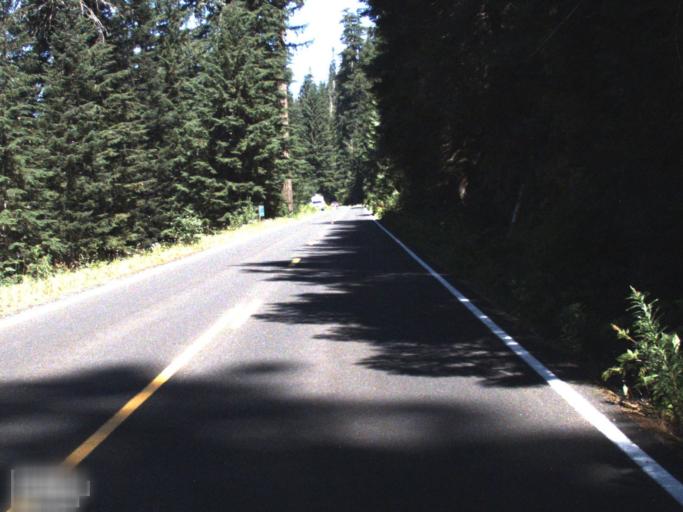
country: US
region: Washington
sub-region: King County
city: Enumclaw
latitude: 46.8157
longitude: -121.5545
